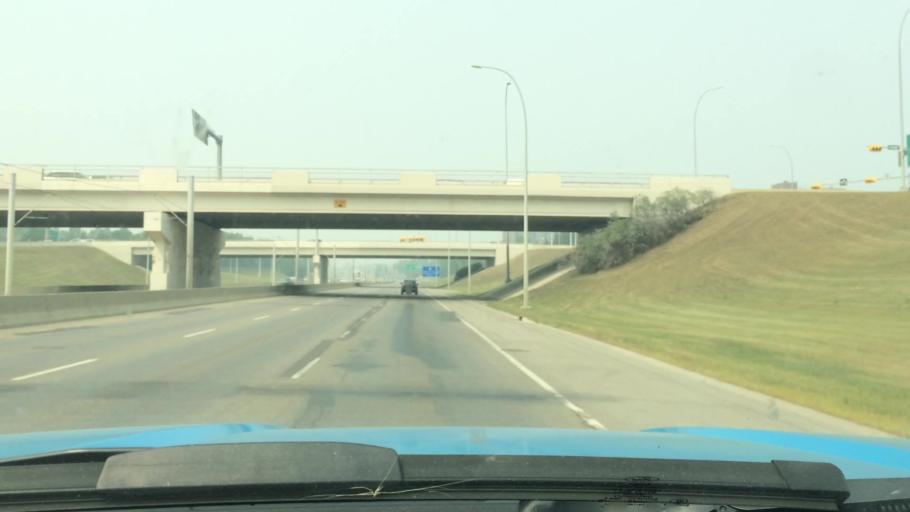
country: CA
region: Alberta
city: Calgary
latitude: 51.0974
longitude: -114.1480
